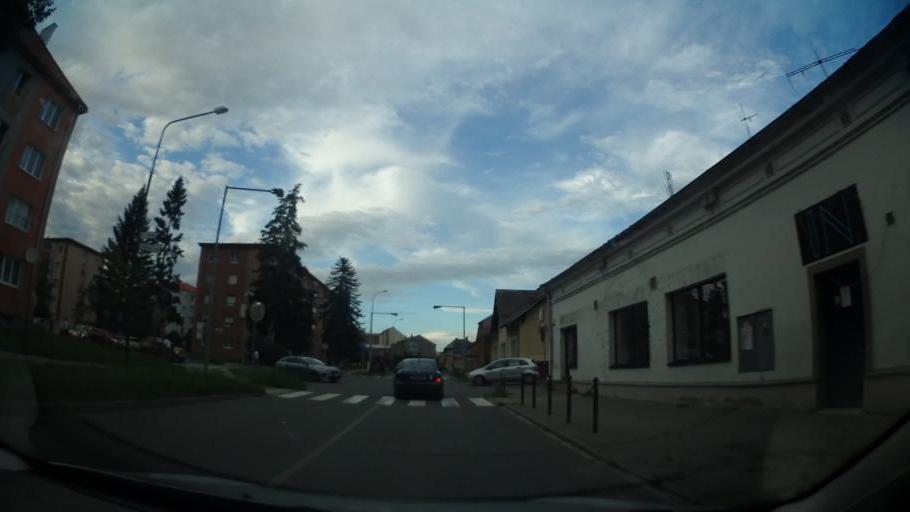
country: CZ
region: Olomoucky
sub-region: Okres Olomouc
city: Unicov
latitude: 49.7676
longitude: 17.1177
